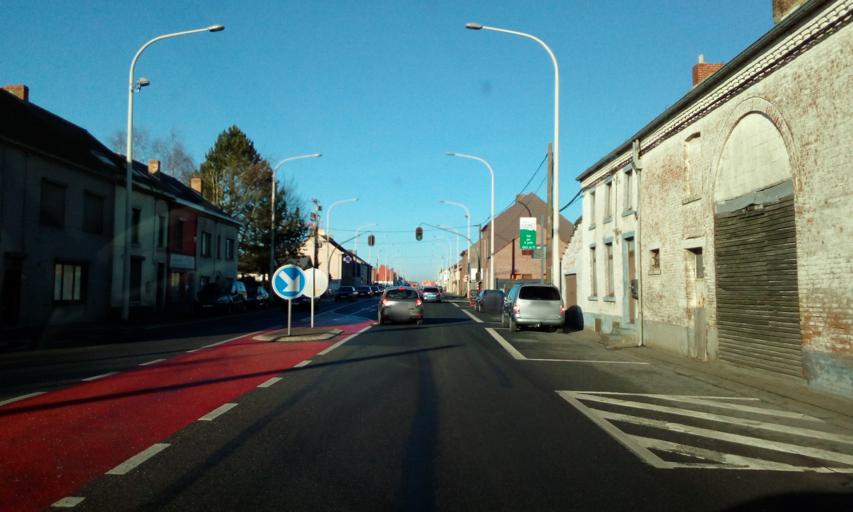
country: BE
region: Wallonia
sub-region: Province du Hainaut
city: Gerpinnes
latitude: 50.3369
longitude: 4.4746
